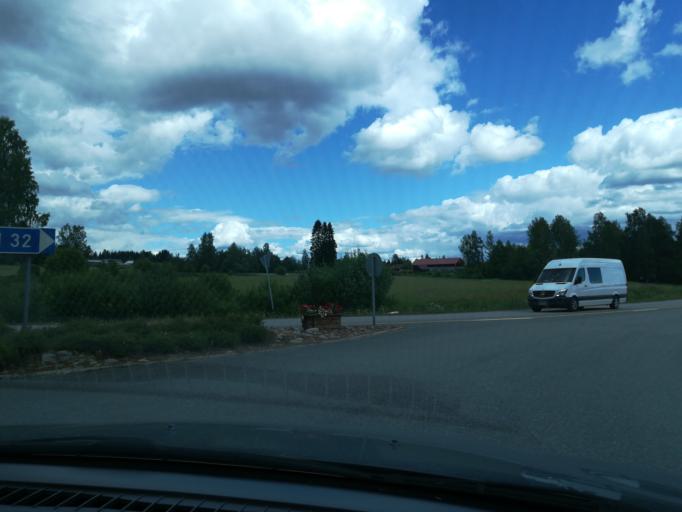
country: FI
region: Southern Savonia
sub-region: Mikkeli
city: Hirvensalmi
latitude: 61.6706
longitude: 26.7642
